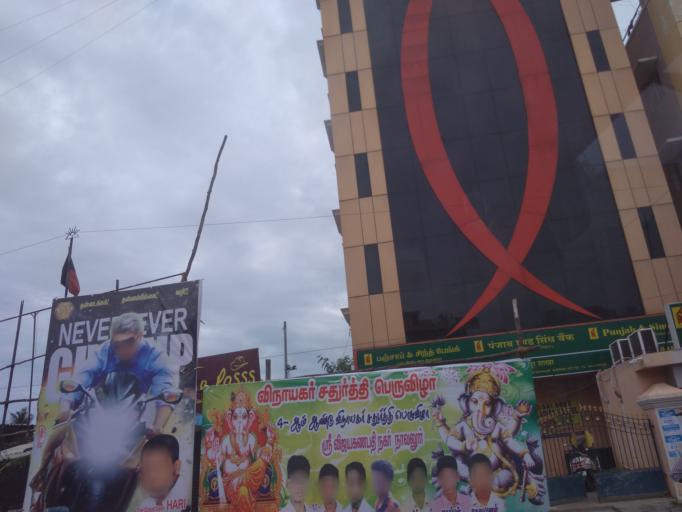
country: IN
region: Tamil Nadu
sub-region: Kancheepuram
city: Injambakkam
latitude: 12.8450
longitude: 80.2267
